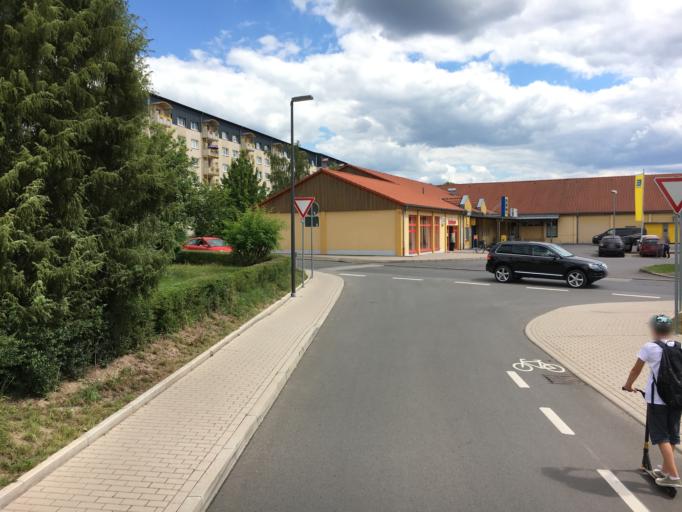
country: DE
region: Thuringia
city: Schmalkalden
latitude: 50.7188
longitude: 10.4658
